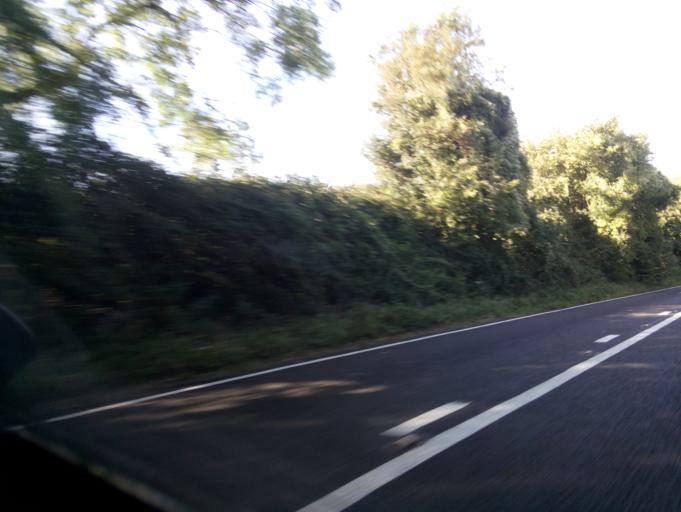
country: GB
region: England
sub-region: Hampshire
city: Four Marks
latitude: 51.0237
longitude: -1.0778
